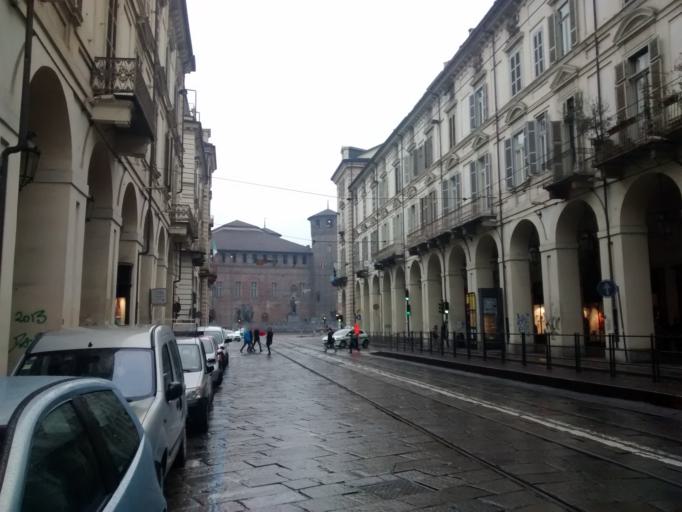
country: IT
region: Piedmont
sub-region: Provincia di Torino
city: Turin
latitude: 45.0697
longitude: 7.6877
